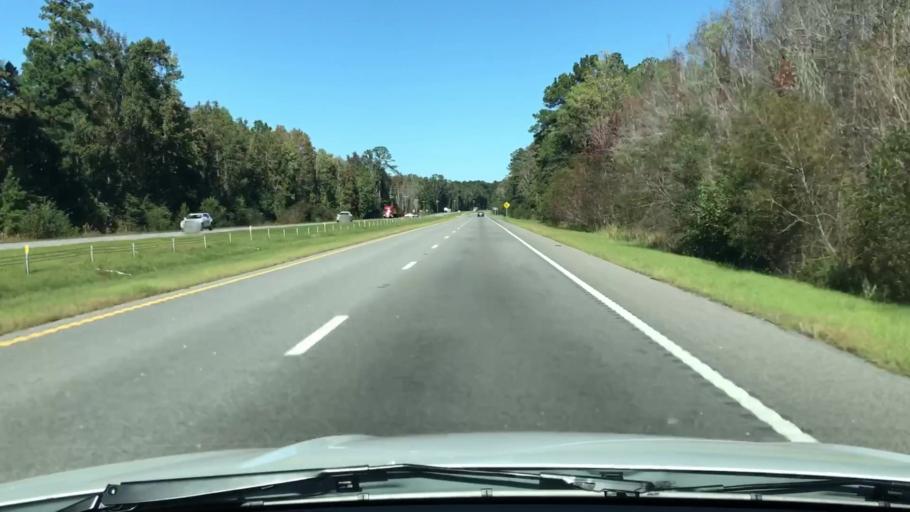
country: US
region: South Carolina
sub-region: Colleton County
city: Walterboro
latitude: 32.7223
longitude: -80.6020
